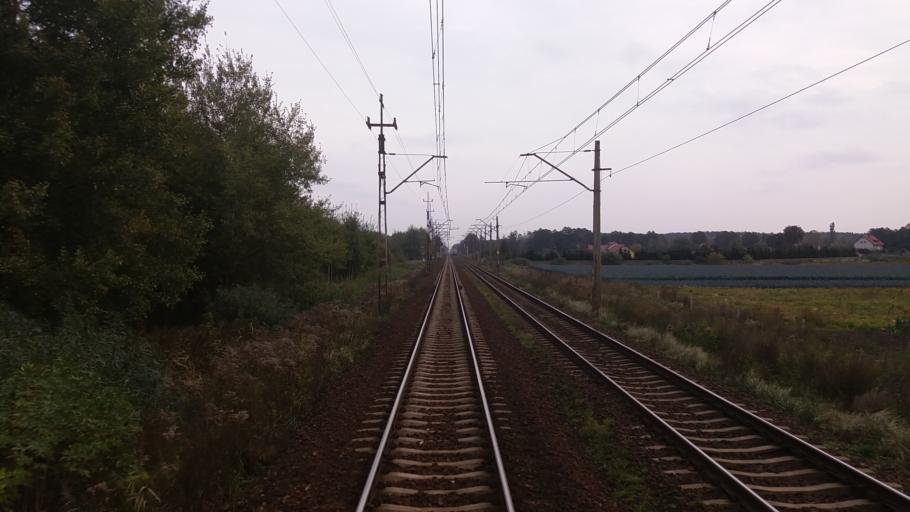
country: PL
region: West Pomeranian Voivodeship
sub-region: Powiat gryfinski
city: Stare Czarnowo
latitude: 53.3863
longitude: 14.7351
